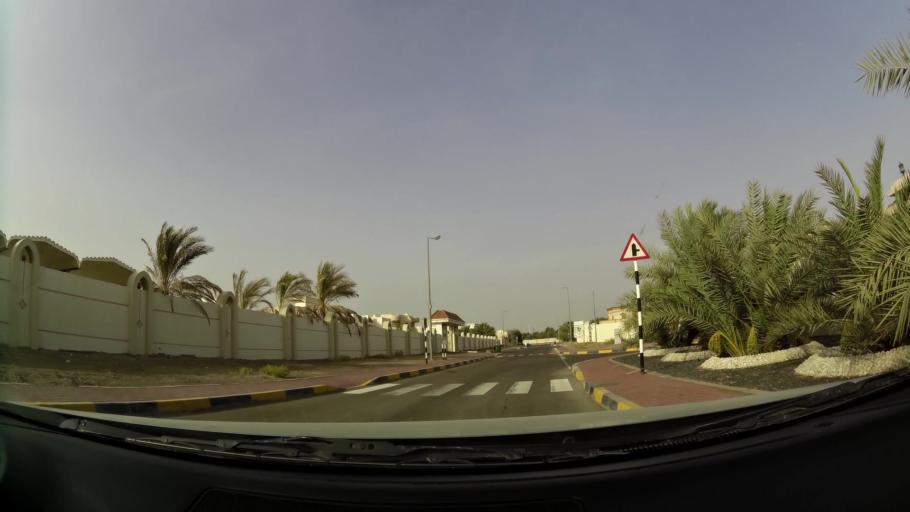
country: AE
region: Abu Dhabi
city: Al Ain
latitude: 24.2190
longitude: 55.6657
